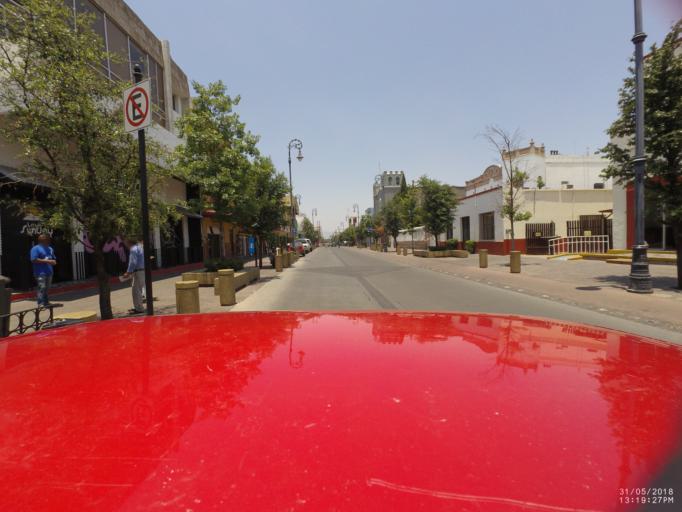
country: MX
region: Aguascalientes
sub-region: Aguascalientes
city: Aguascalientes
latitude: 21.8824
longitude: -102.2912
